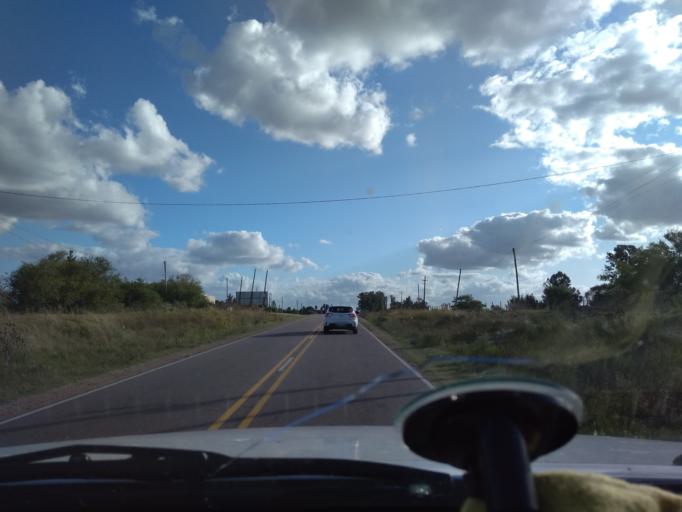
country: UY
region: Canelones
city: Tala
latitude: -34.3676
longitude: -55.7817
